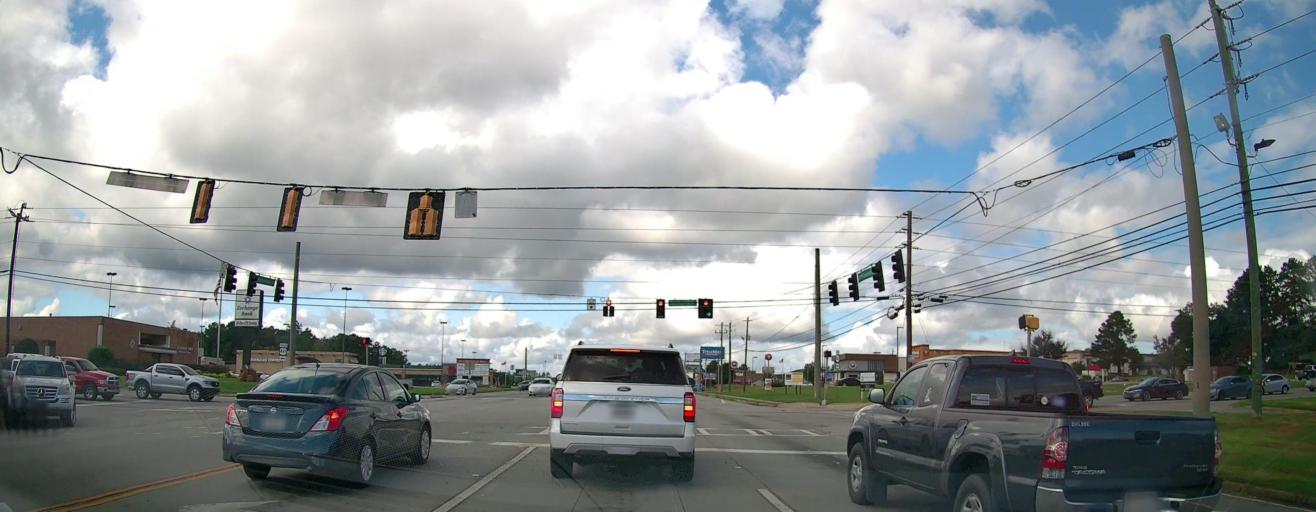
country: US
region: Georgia
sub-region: Baldwin County
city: Milledgeville
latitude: 33.1089
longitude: -83.2546
